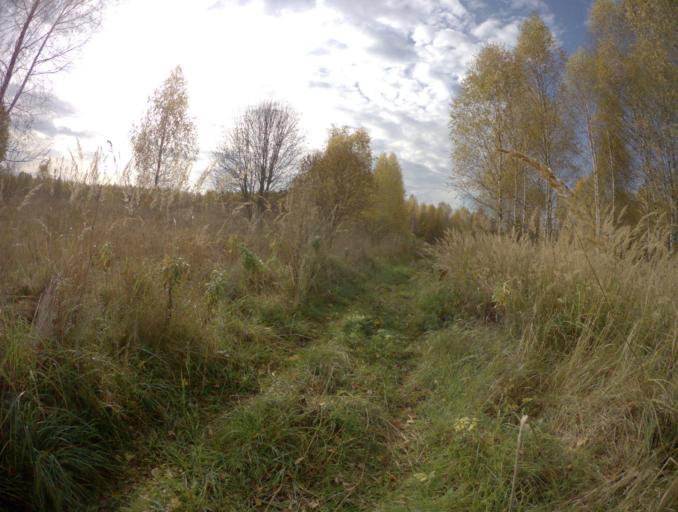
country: RU
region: Vladimir
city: Golovino
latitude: 55.9701
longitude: 40.3829
